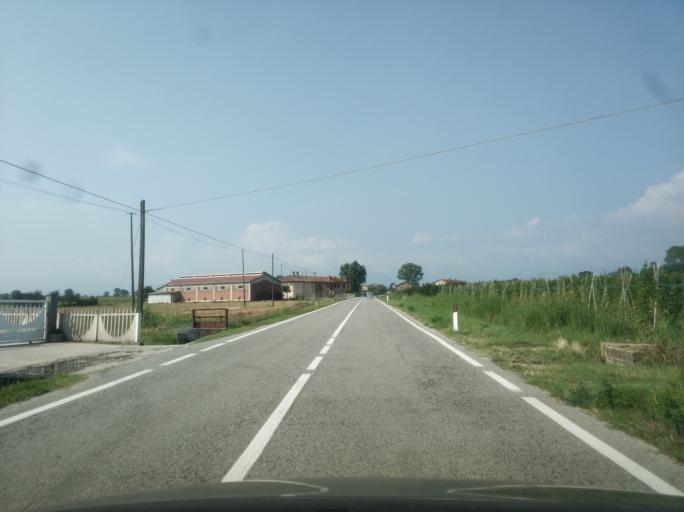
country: IT
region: Piedmont
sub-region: Provincia di Cuneo
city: Tarantasca
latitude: 44.4924
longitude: 7.5561
